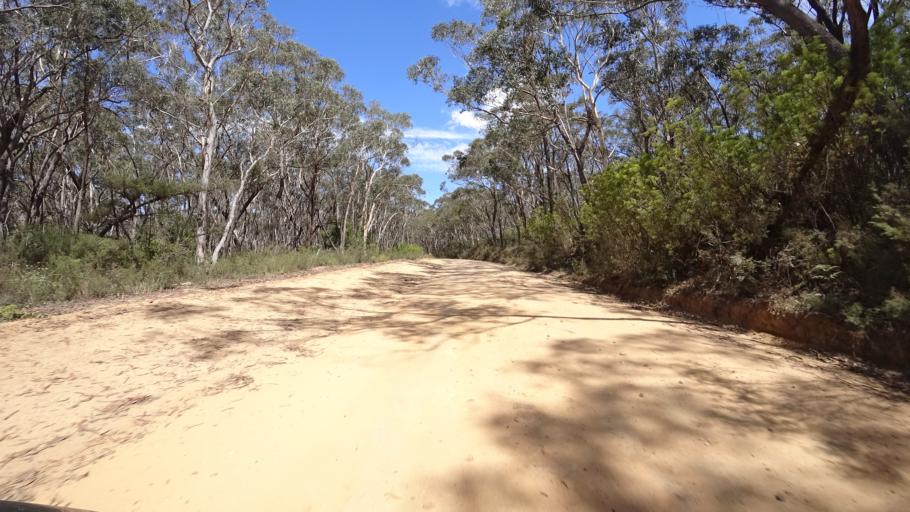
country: AU
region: New South Wales
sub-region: Lithgow
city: Lithgow
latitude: -33.2887
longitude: 150.2336
